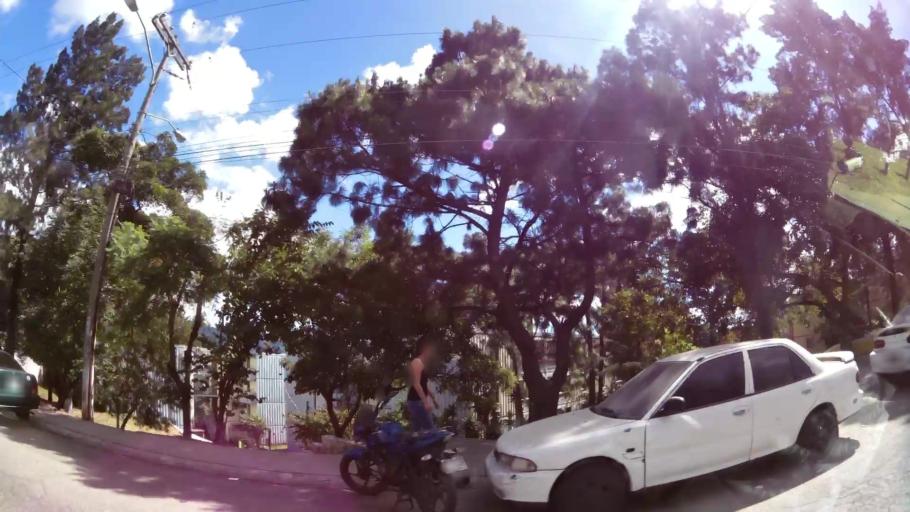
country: GT
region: Guatemala
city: Petapa
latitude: 14.5439
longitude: -90.5488
